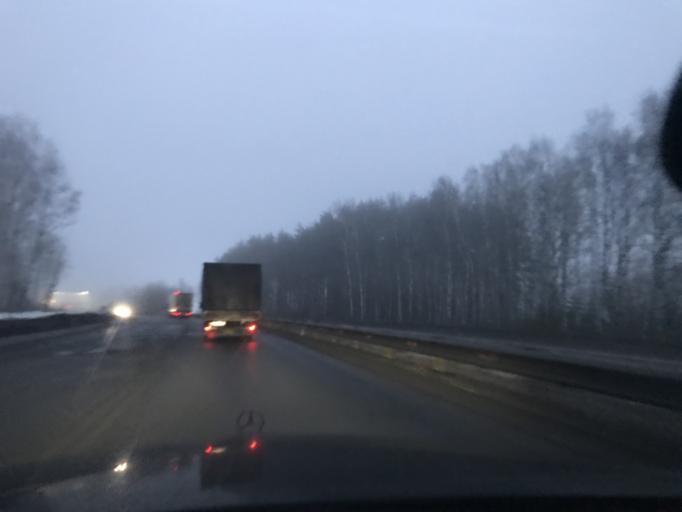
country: RU
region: Vladimir
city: Novovyazniki
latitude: 56.2036
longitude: 42.2919
